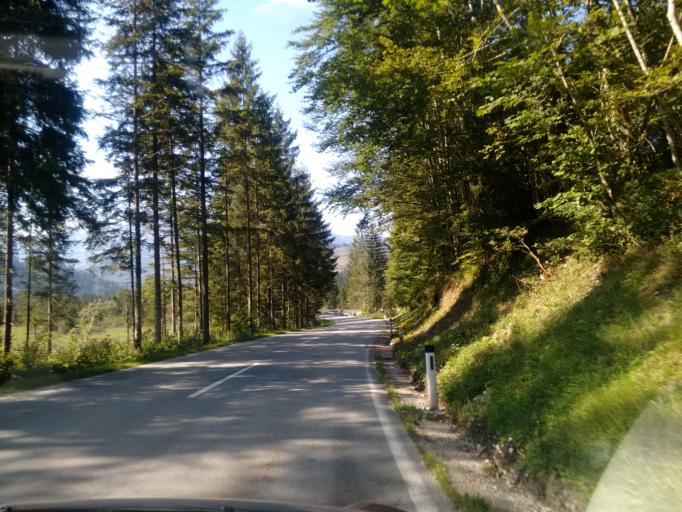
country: AT
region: Upper Austria
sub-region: Politischer Bezirk Gmunden
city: Gruenau im Almtal
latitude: 47.7737
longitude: 13.9591
